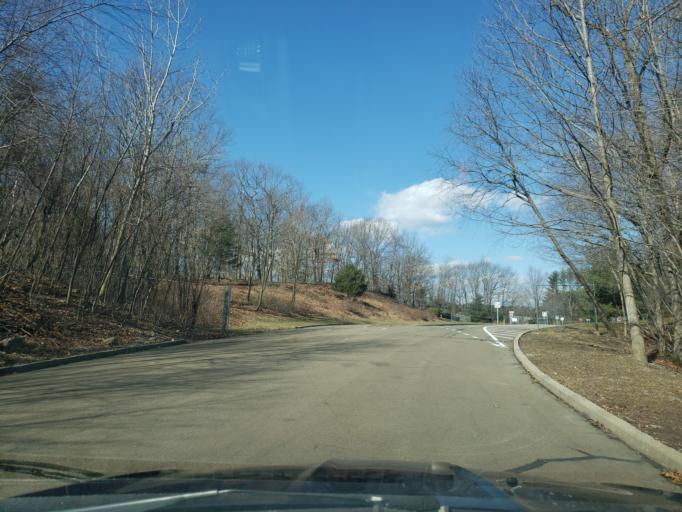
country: US
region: Connecticut
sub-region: New Haven County
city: West Haven
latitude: 41.3010
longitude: -72.9821
